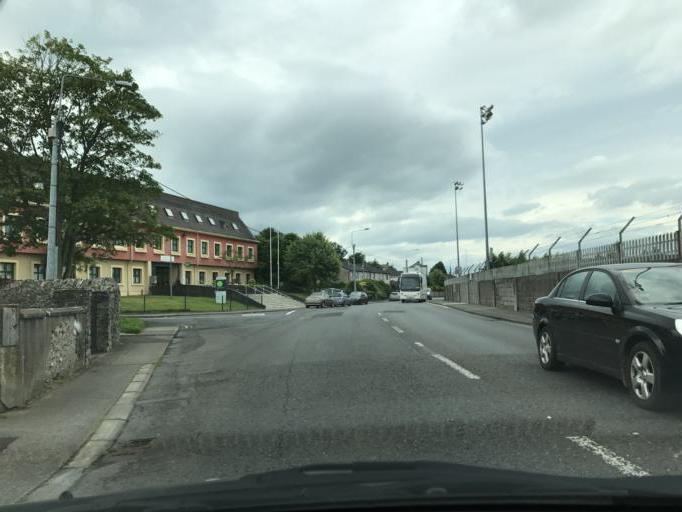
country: IE
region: Connaught
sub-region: Sligo
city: Sligo
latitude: 54.2680
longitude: -8.4625
